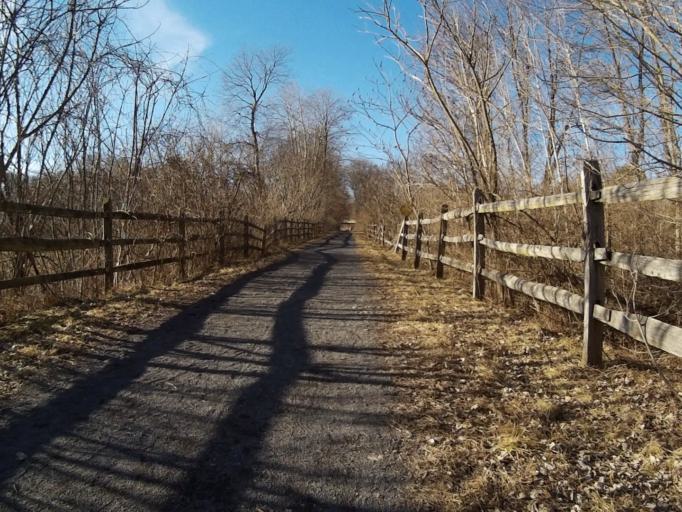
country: US
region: Pennsylvania
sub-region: Centre County
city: State College
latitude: 40.8172
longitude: -77.8777
